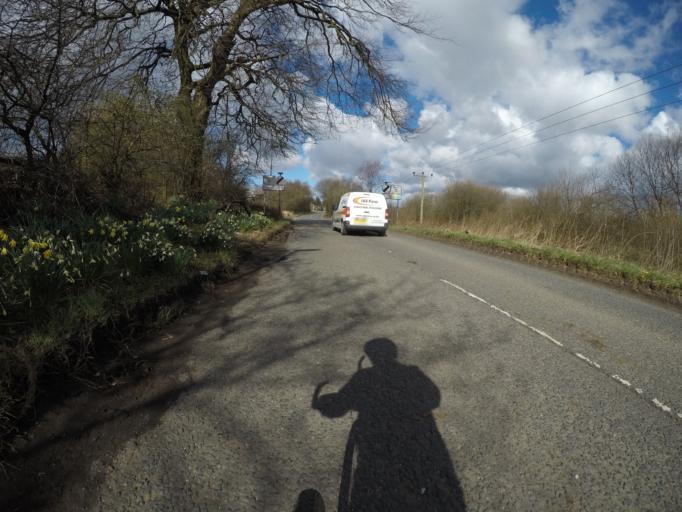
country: GB
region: Scotland
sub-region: North Ayrshire
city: Beith
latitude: 55.7312
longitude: -4.6070
